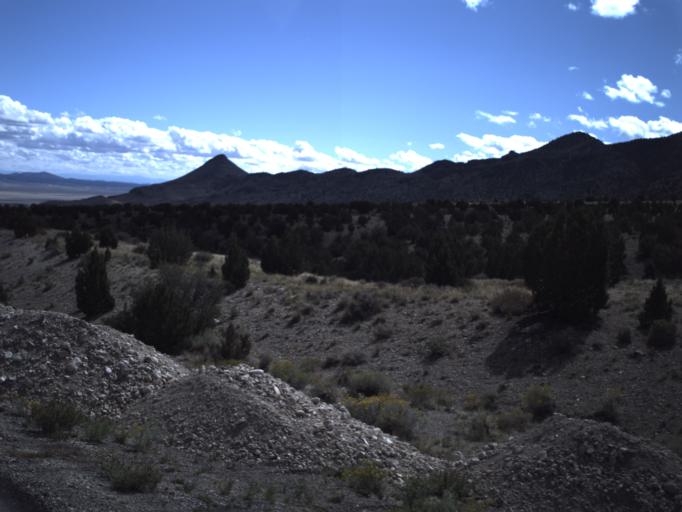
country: US
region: Utah
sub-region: Beaver County
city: Milford
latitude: 38.5104
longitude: -113.5230
